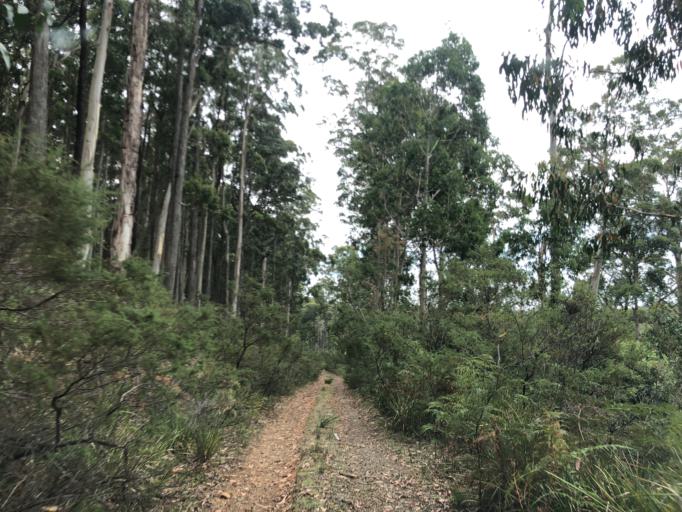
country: AU
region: Victoria
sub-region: Moorabool
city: Bacchus Marsh
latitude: -37.4450
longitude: 144.2460
